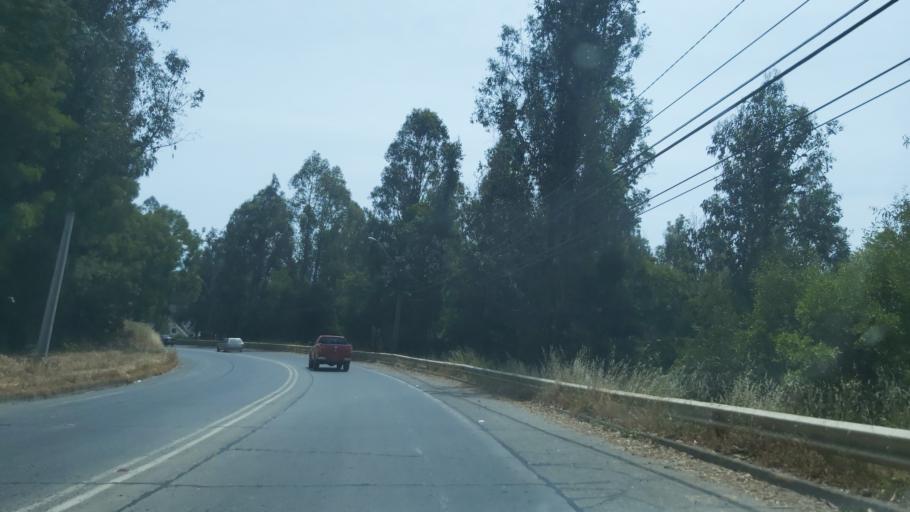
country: CL
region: Maule
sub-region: Provincia de Talca
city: Constitucion
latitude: -35.3460
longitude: -72.4140
